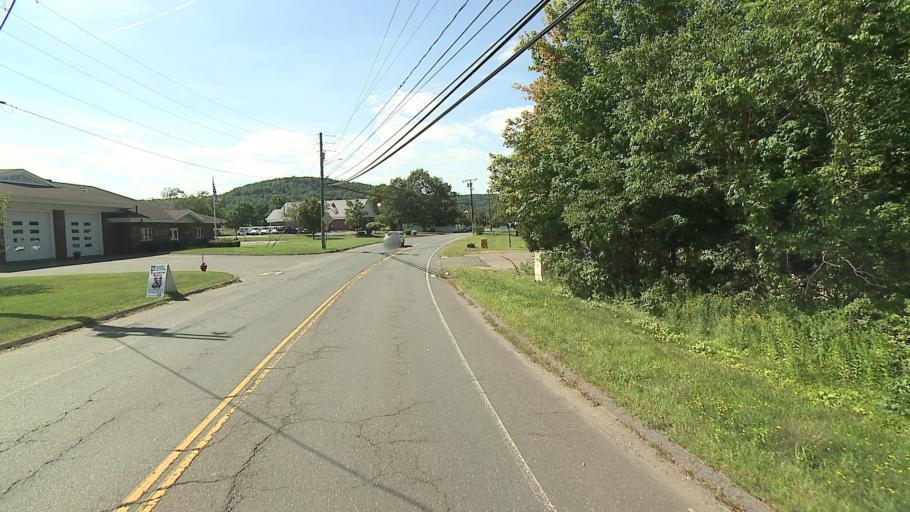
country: US
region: Connecticut
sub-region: Hartford County
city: West Simsbury
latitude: 41.8712
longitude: -72.8530
